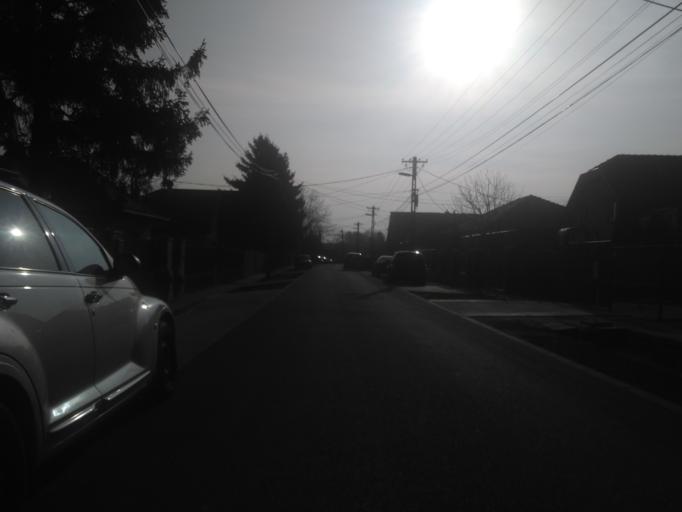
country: HU
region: Pest
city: Gyal
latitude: 47.3992
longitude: 19.2493
